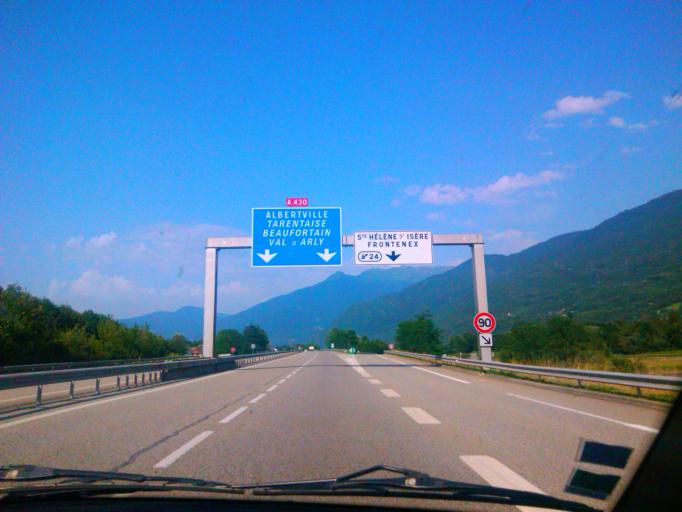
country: FR
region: Rhone-Alpes
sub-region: Departement de la Savoie
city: Sainte-Helene-sur-Isere
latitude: 45.6224
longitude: 6.3173
